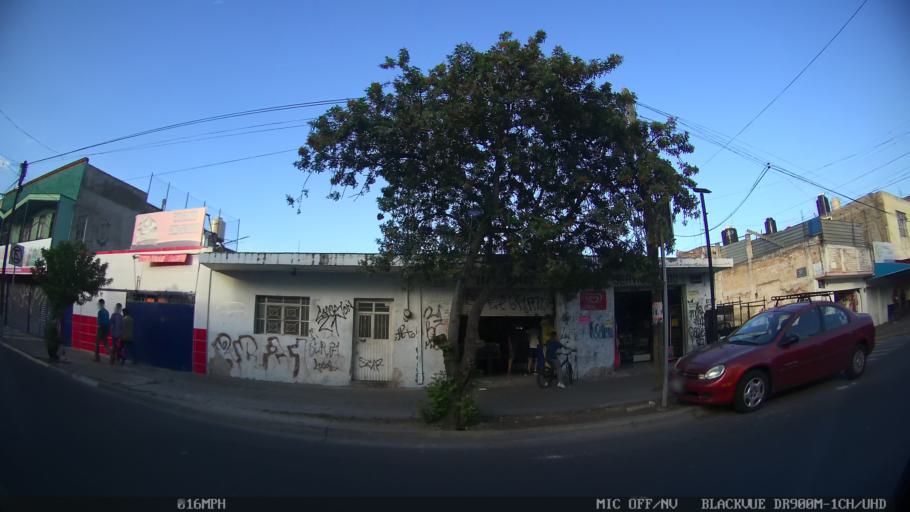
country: MX
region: Jalisco
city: Tlaquepaque
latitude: 20.7087
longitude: -103.2943
